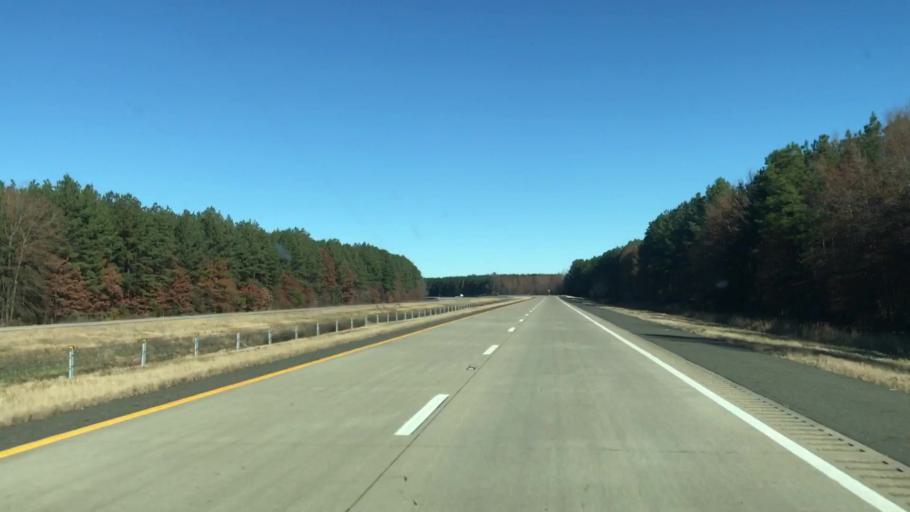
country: US
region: Texas
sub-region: Bowie County
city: Texarkana
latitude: 33.2351
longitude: -93.8731
